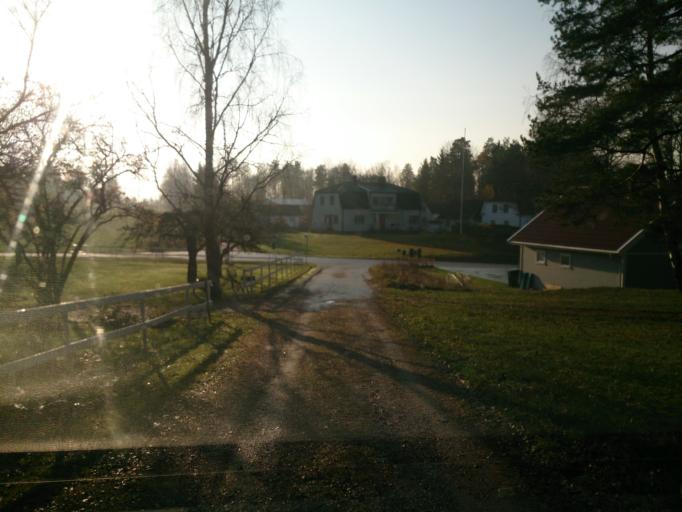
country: SE
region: OEstergoetland
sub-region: Atvidabergs Kommun
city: Atvidaberg
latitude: 58.3400
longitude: 16.0273
